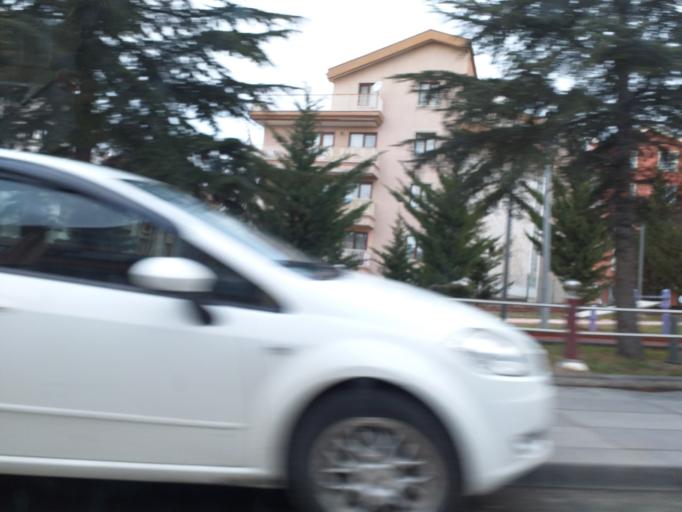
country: TR
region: Ankara
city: Ankara
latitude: 39.9773
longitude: 32.8192
